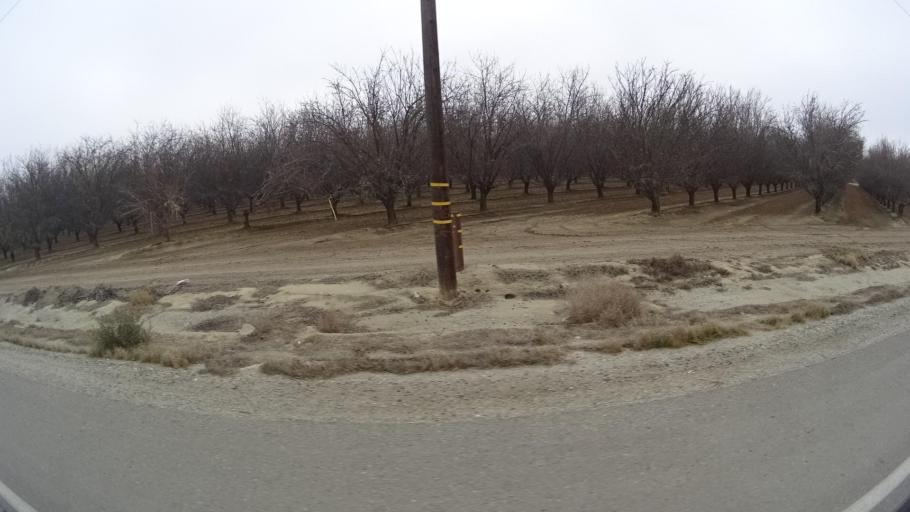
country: US
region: California
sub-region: Kern County
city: Greenfield
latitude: 35.0929
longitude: -119.1110
